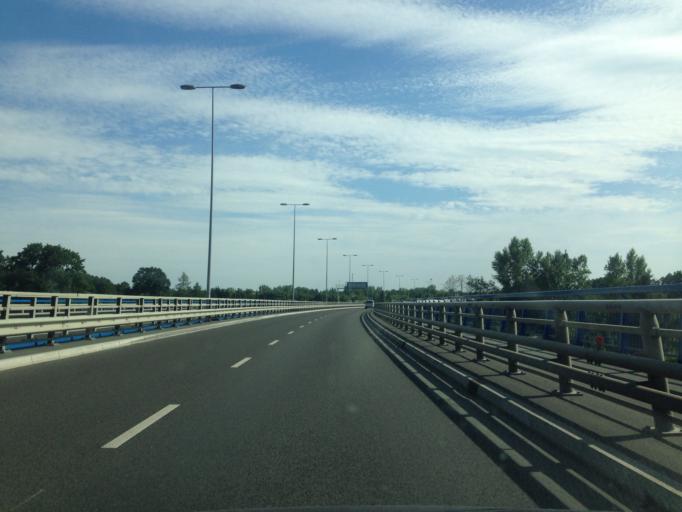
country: PL
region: Kujawsko-Pomorskie
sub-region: Torun
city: Torun
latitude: 53.0068
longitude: 18.6575
